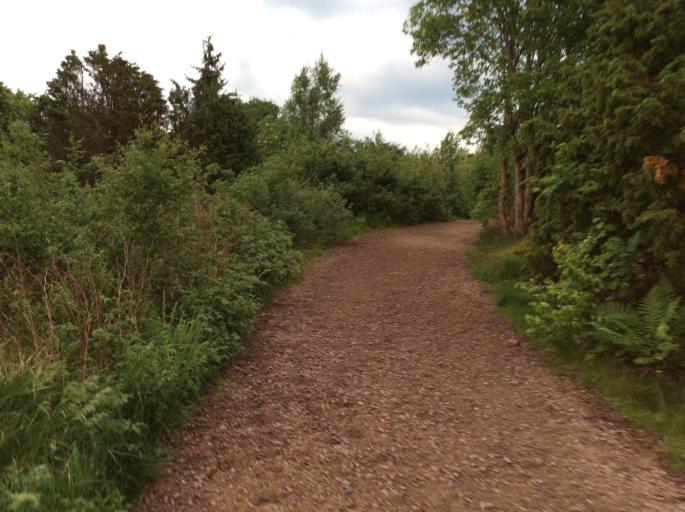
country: SE
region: Vaestra Goetaland
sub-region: Goteborg
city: Majorna
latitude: 57.8023
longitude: 11.8855
